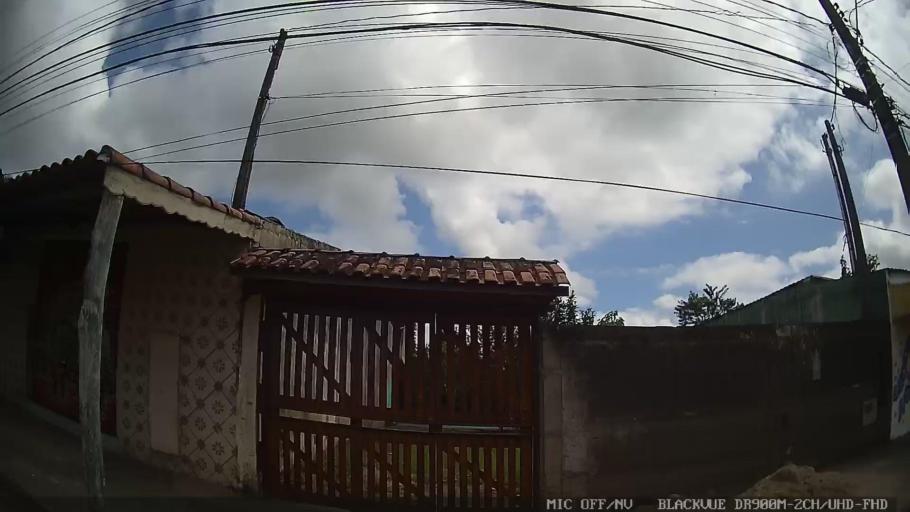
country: BR
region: Sao Paulo
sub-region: Peruibe
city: Peruibe
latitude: -24.2929
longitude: -47.0195
